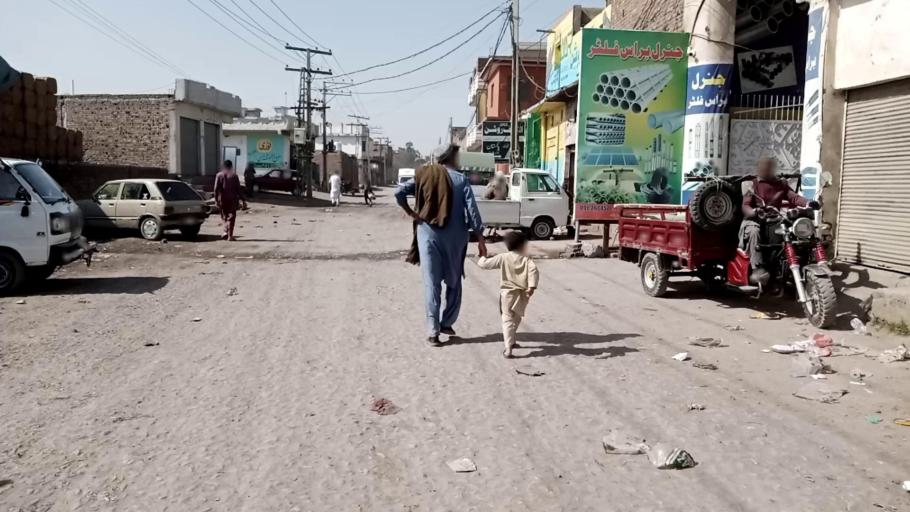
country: PK
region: Khyber Pakhtunkhwa
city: Peshawar
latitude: 34.0183
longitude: 71.6466
